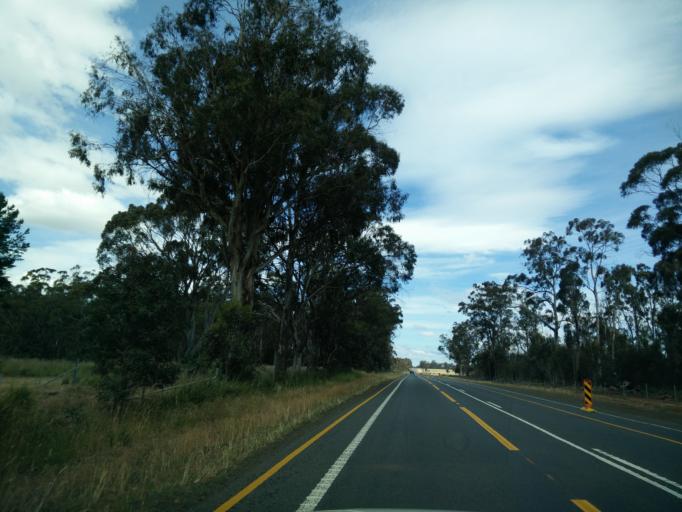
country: AU
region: Tasmania
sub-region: Northern Midlands
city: Evandale
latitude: -41.7362
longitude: 147.3275
